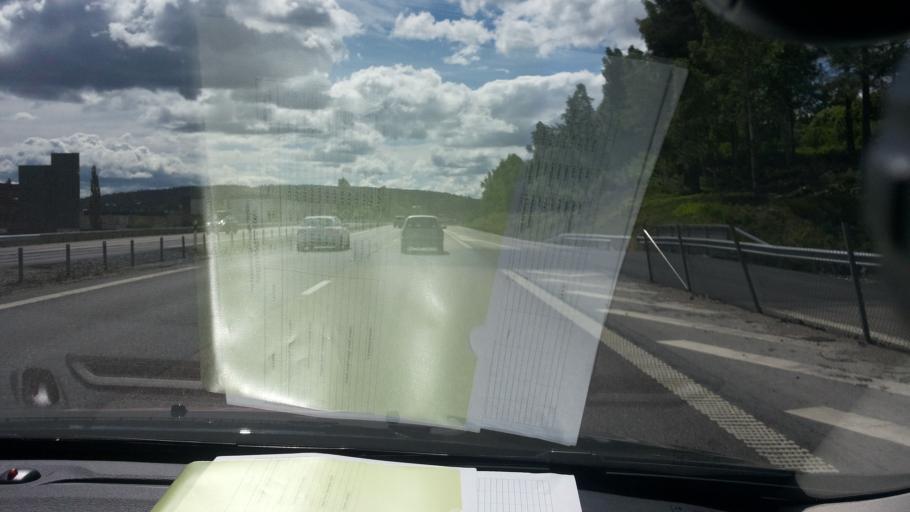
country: SE
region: Vaesternorrland
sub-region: Timra Kommun
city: Timra
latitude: 62.4888
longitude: 17.3236
